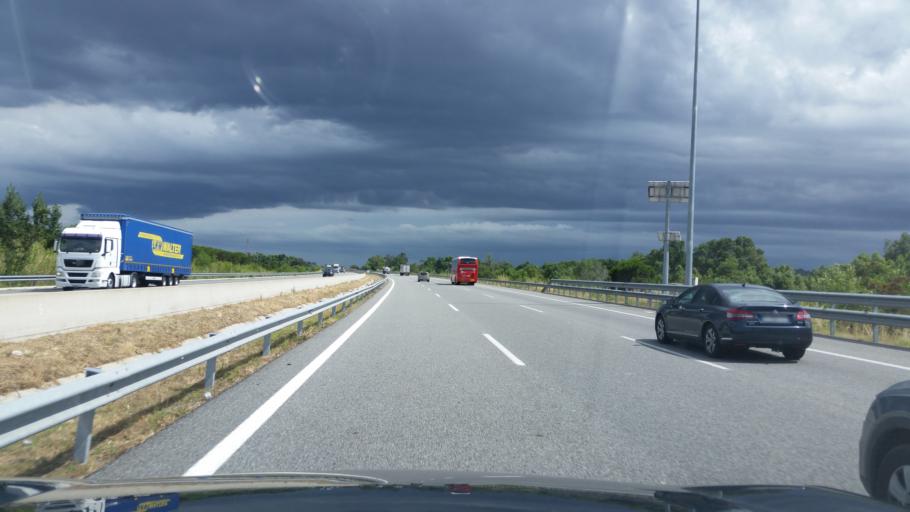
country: ES
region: Catalonia
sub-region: Provincia de Girona
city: Biure
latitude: 42.3403
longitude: 2.9209
